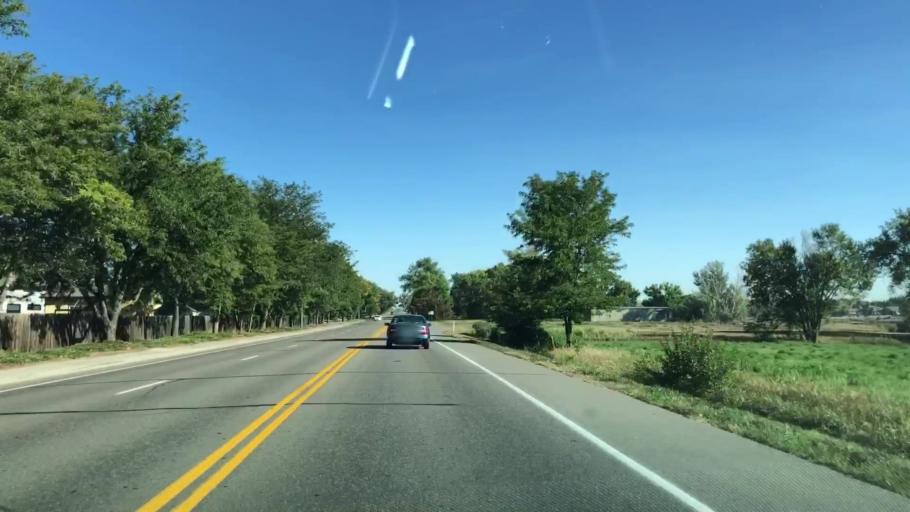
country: US
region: Colorado
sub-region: Larimer County
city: Loveland
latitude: 40.4190
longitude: -105.0587
